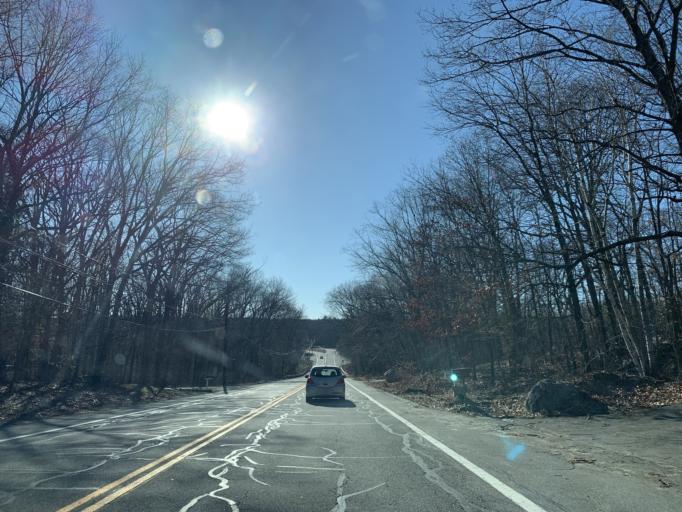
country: US
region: Rhode Island
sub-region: Providence County
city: North Providence
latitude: 41.8810
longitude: -71.4693
